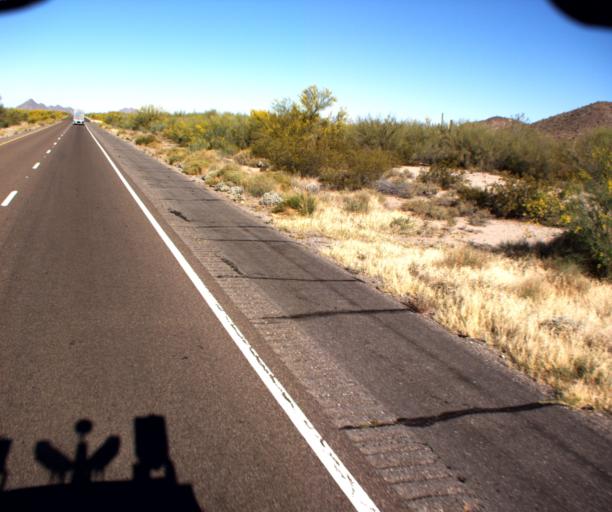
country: US
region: Arizona
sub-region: Maricopa County
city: Gila Bend
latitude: 32.8673
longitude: -112.4211
